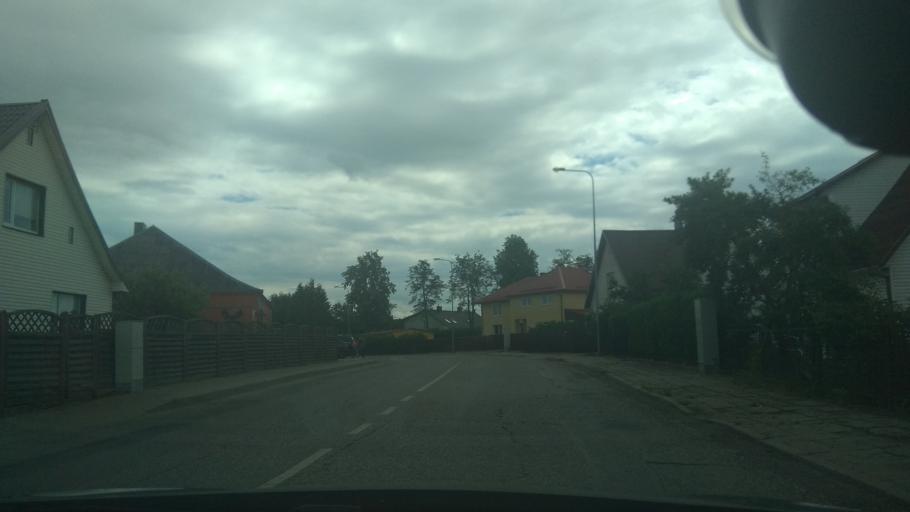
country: LT
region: Marijampoles apskritis
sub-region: Marijampole Municipality
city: Marijampole
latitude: 54.5502
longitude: 23.3534
